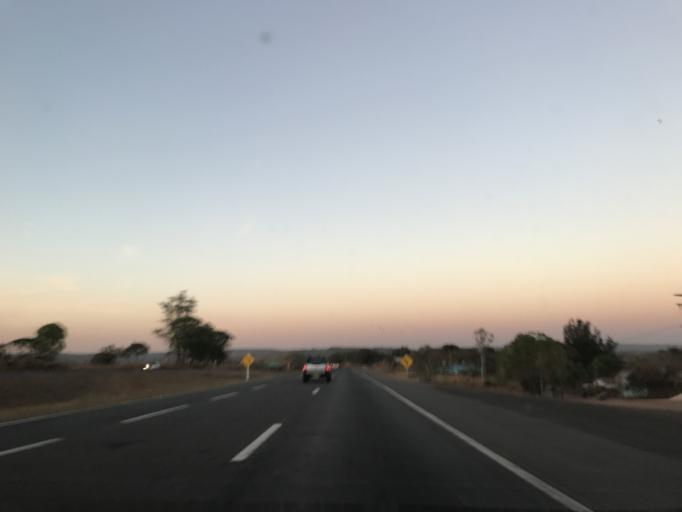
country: BR
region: Goias
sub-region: Abadiania
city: Abadiania
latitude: -16.1279
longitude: -48.5956
